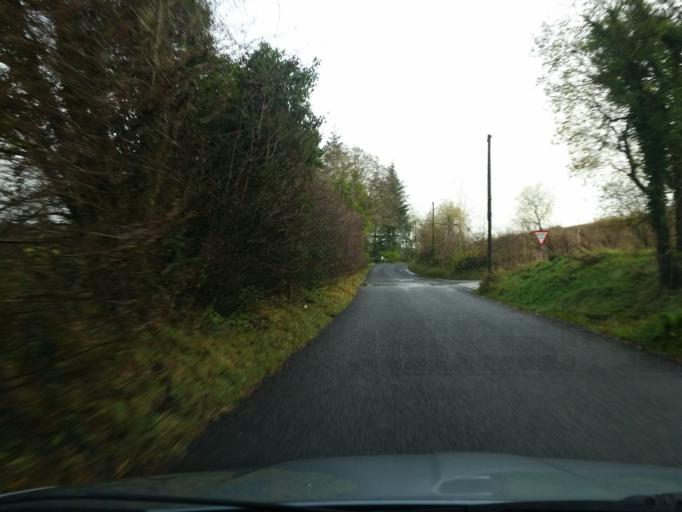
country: GB
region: Northern Ireland
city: Lisnaskea
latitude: 54.2466
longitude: -7.3843
